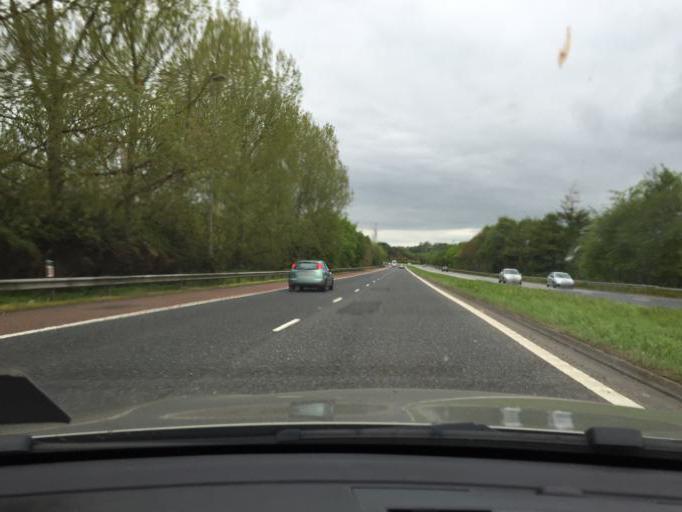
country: GB
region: Northern Ireland
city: Hillsborough
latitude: 54.4205
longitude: -6.1407
